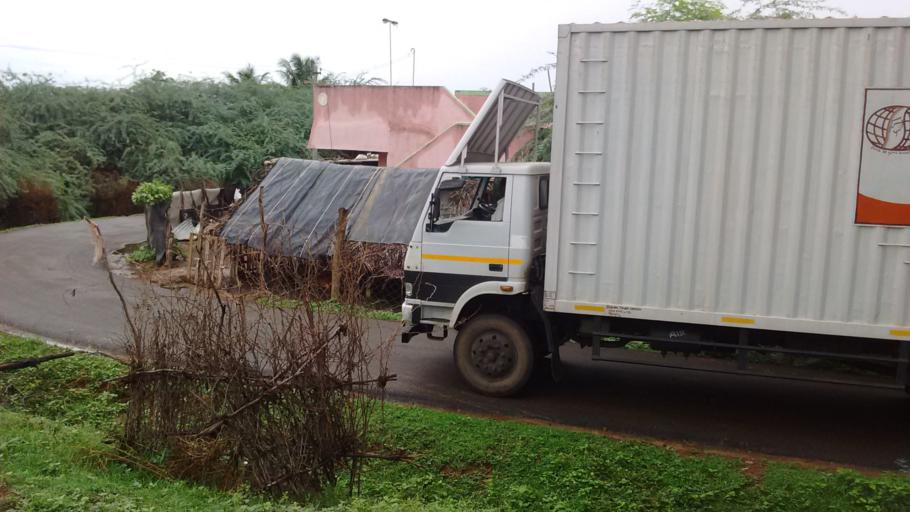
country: IN
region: Tamil Nadu
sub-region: Kancheepuram
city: Sriperumbudur
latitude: 12.9157
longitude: 79.9565
